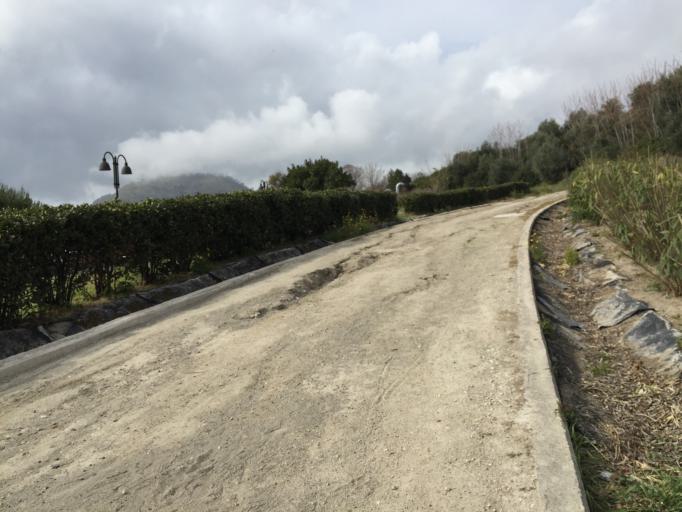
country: IT
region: Campania
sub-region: Provincia di Napoli
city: Pozzuoli
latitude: 40.8322
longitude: 14.1293
